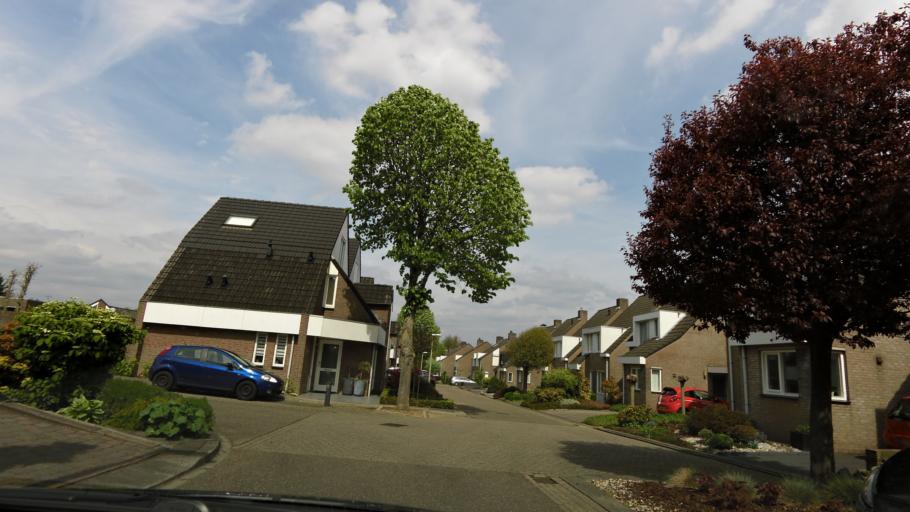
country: NL
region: Limburg
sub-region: Gemeente Heerlen
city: Heerlen
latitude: 50.8746
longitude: 5.9595
